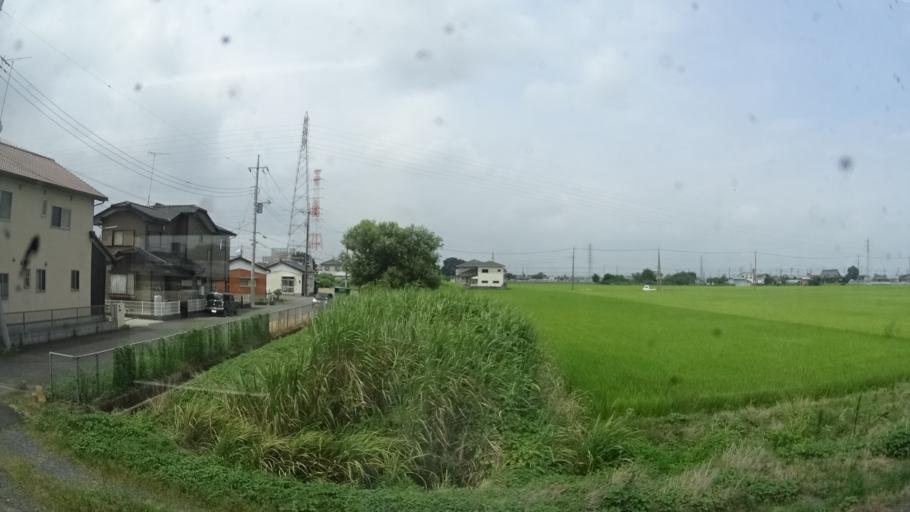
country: JP
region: Ibaraki
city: Shimodate
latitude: 36.3114
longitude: 139.9717
